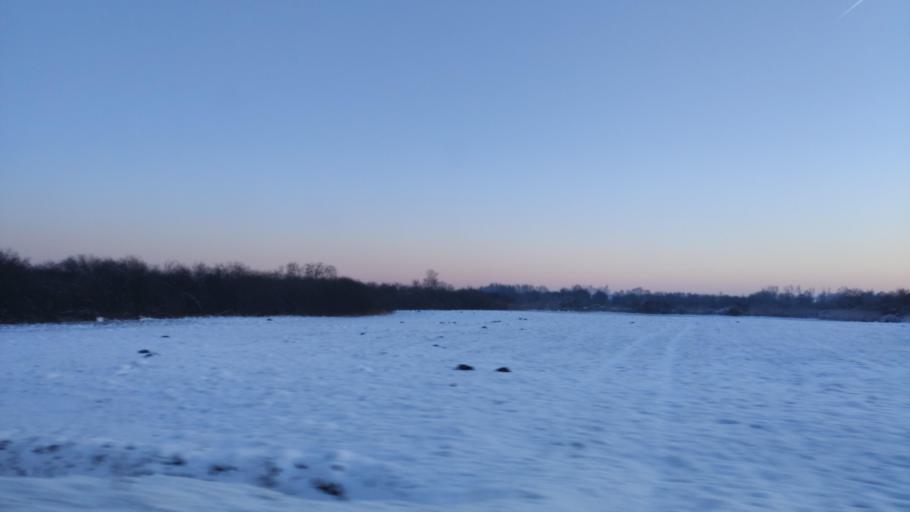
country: PL
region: Kujawsko-Pomorskie
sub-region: Powiat zninski
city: Barcin
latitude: 52.8764
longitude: 17.8723
